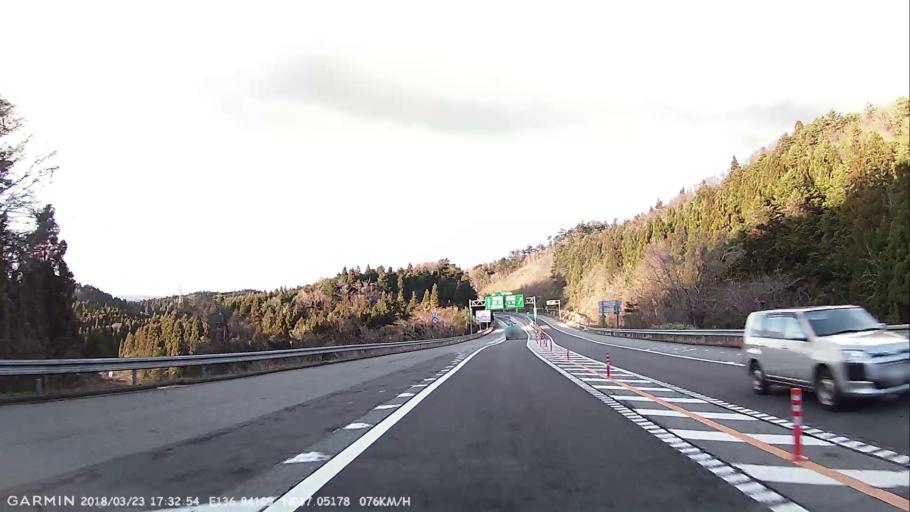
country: JP
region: Ishikawa
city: Nanao
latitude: 37.0521
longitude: 136.8413
